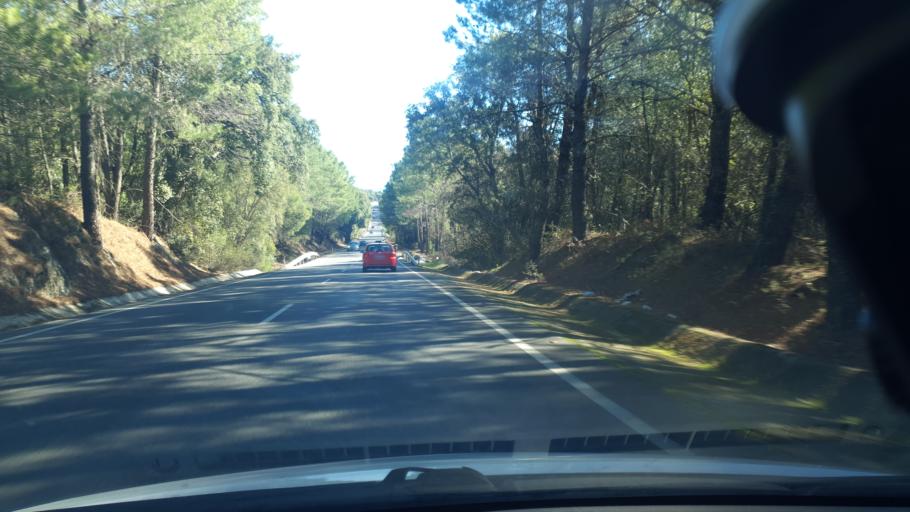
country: ES
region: Castille and Leon
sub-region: Provincia de Avila
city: Piedralaves
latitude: 40.3148
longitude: -4.6727
